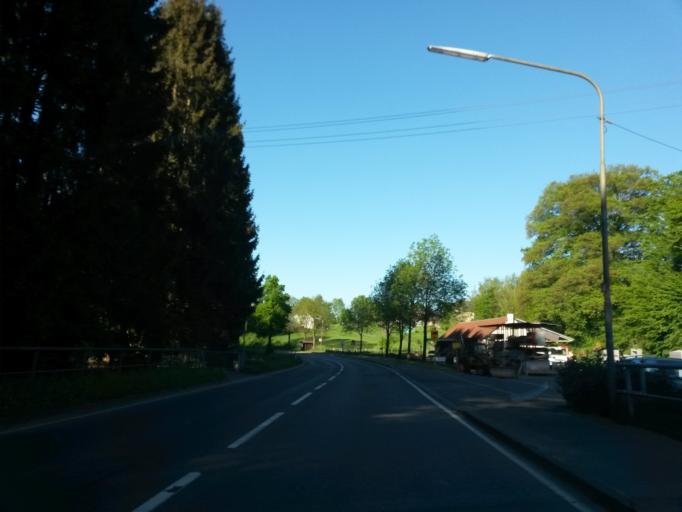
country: DE
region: North Rhine-Westphalia
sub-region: Regierungsbezirk Koln
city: Much
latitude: 50.8881
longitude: 7.3602
